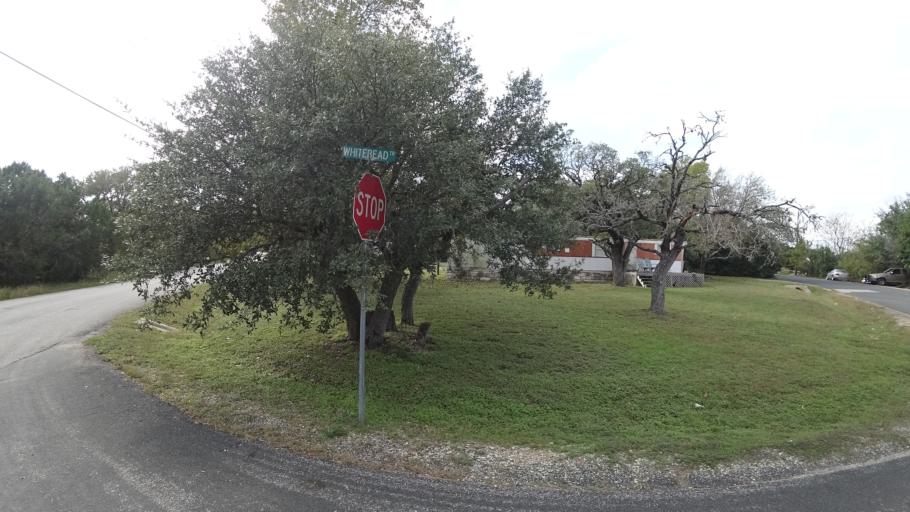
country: US
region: Texas
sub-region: Travis County
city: Hudson Bend
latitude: 30.3794
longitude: -97.9276
